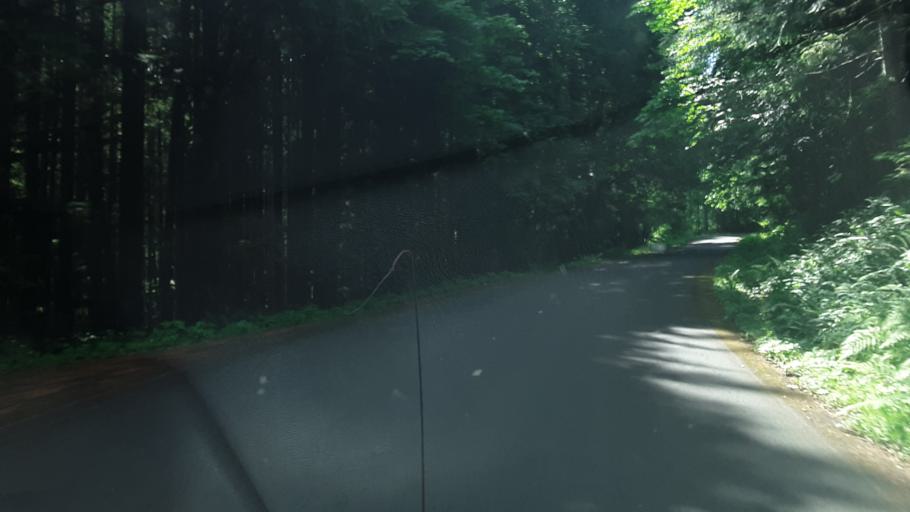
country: US
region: Washington
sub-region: Lewis County
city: Morton
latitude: 46.4085
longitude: -121.9902
